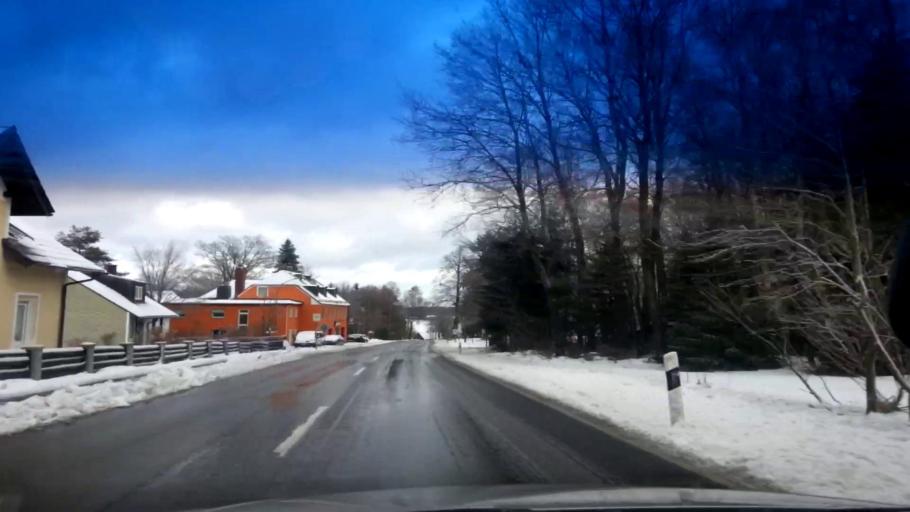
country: DE
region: Bavaria
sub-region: Upper Franconia
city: Kirchenlamitz
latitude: 50.1423
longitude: 11.9287
